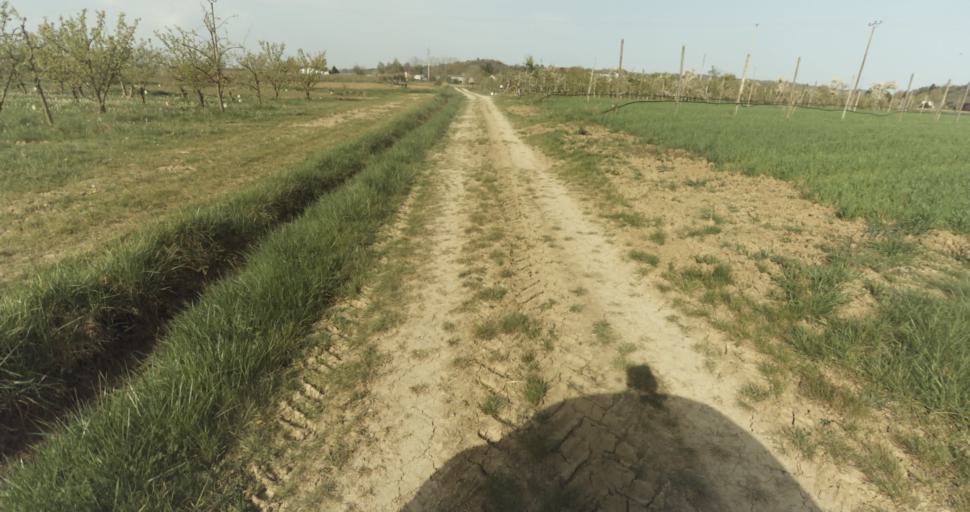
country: FR
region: Midi-Pyrenees
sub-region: Departement du Tarn-et-Garonne
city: Moissac
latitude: 44.1086
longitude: 1.1217
